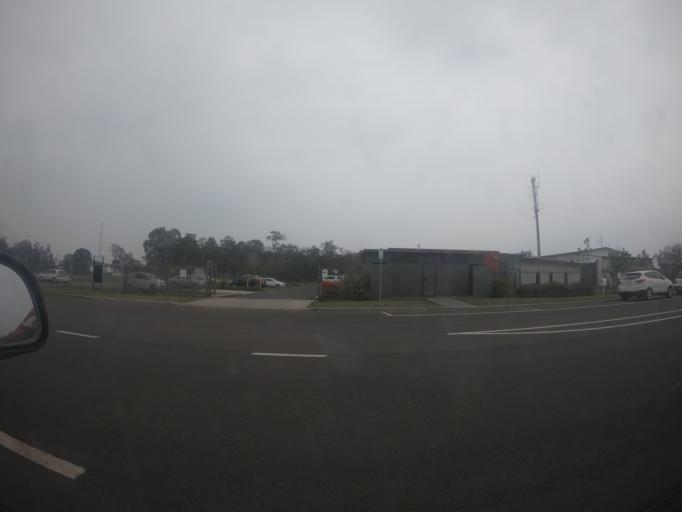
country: AU
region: New South Wales
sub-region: Shellharbour
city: Albion Park Rail
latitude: -34.5592
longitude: 150.7903
